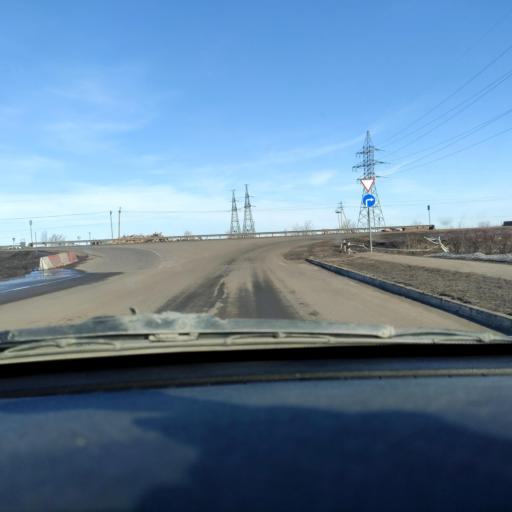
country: RU
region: Samara
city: Podstepki
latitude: 53.5598
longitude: 49.2045
